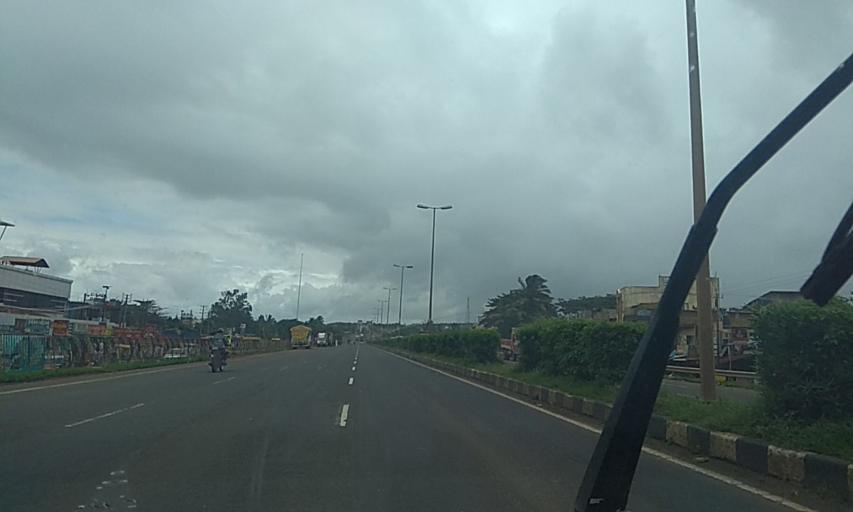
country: IN
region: Karnataka
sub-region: Belgaum
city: Belgaum
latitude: 15.8626
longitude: 74.5309
